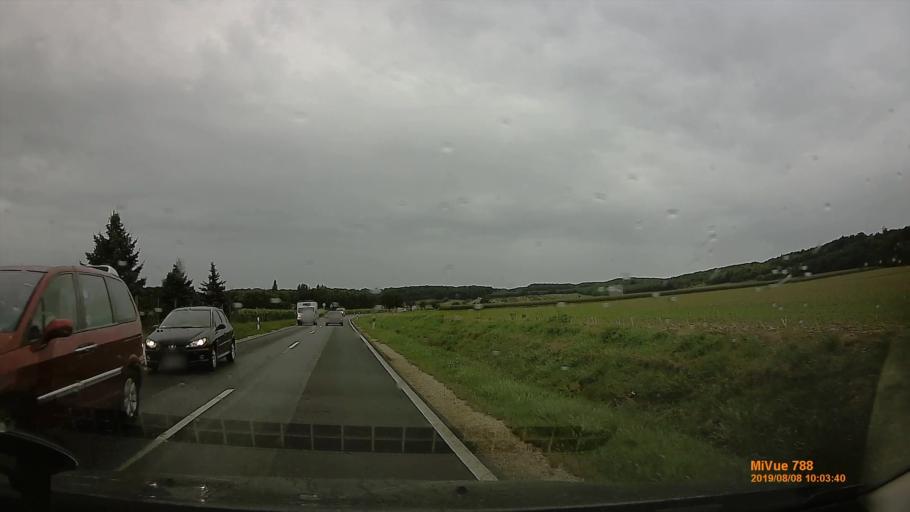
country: HU
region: Zala
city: Zalaegerszeg
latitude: 46.9260
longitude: 16.8580
